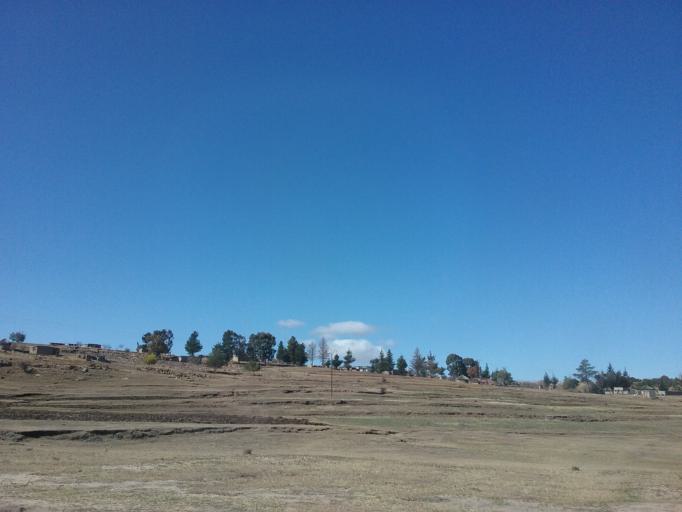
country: LS
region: Maseru
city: Maseru
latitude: -29.4702
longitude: 27.5770
